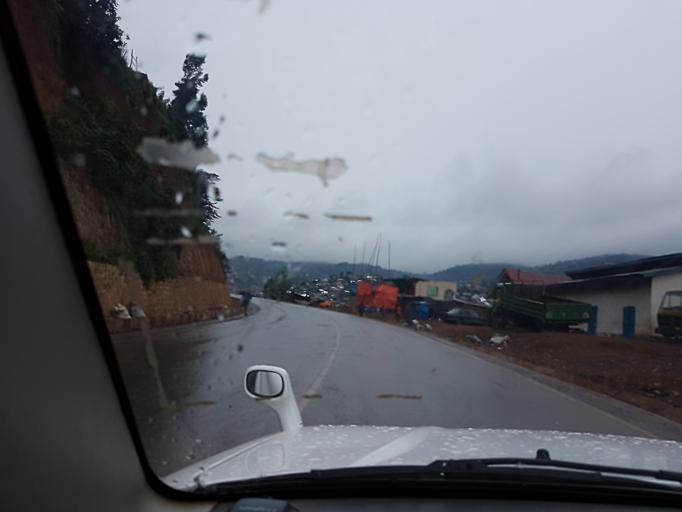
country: CD
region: South Kivu
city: Bukavu
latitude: -2.5113
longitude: 28.8549
